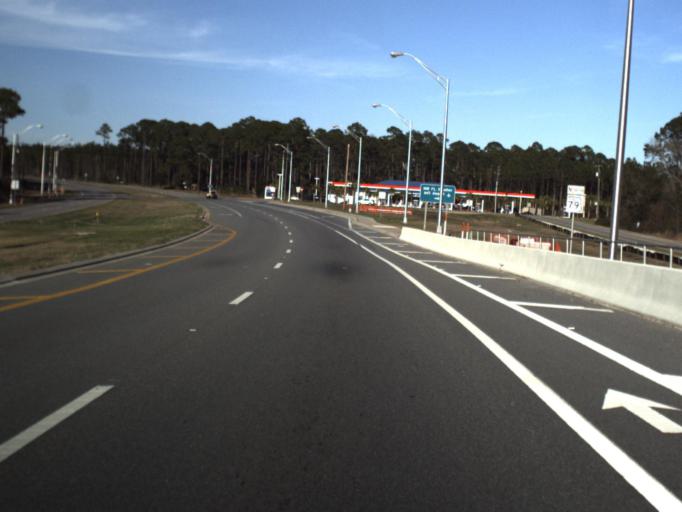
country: US
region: Florida
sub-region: Bay County
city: Laguna Beach
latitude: 30.2975
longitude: -85.8543
